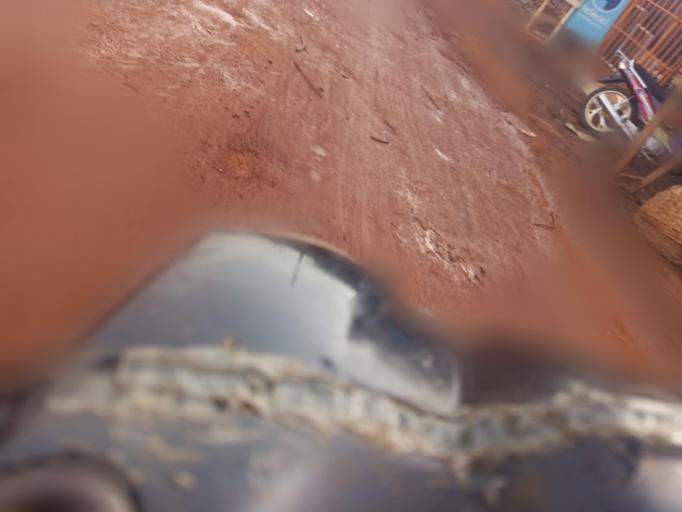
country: ML
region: Bamako
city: Bamako
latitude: 12.5303
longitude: -7.9947
